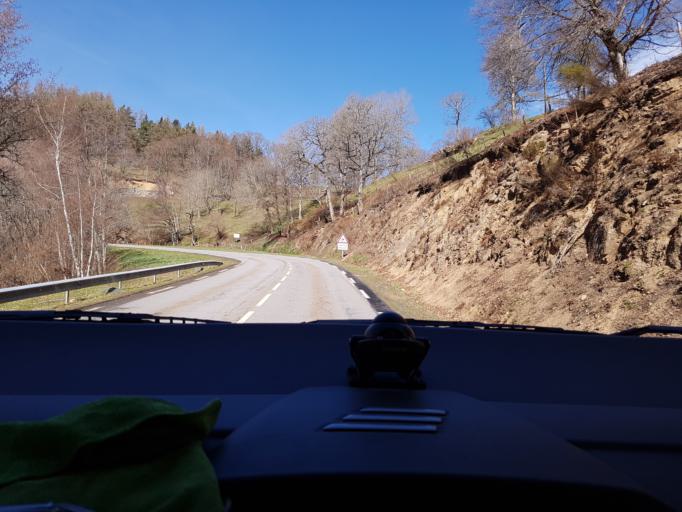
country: FR
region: Auvergne
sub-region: Departement du Cantal
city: Chaudes-Aigues
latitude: 44.8419
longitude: 3.0017
